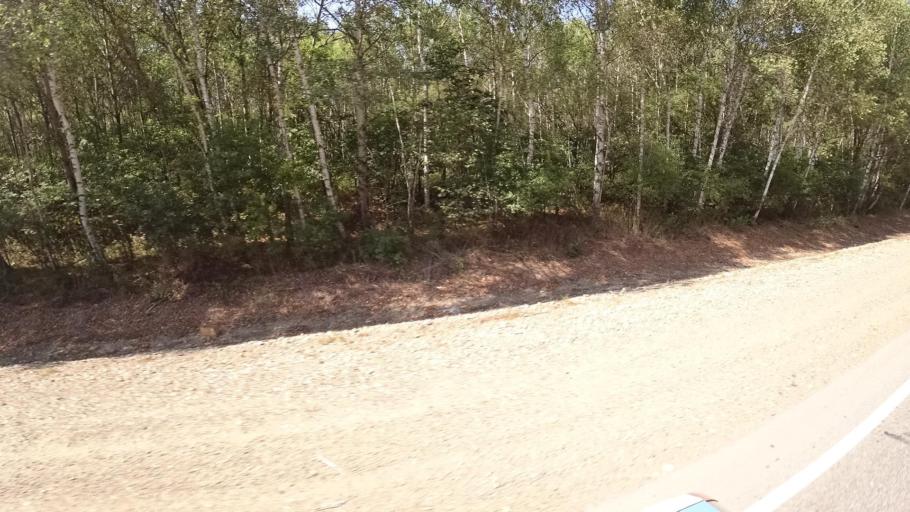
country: RU
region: Khabarovsk Krai
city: Khor
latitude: 47.9865
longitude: 135.0899
